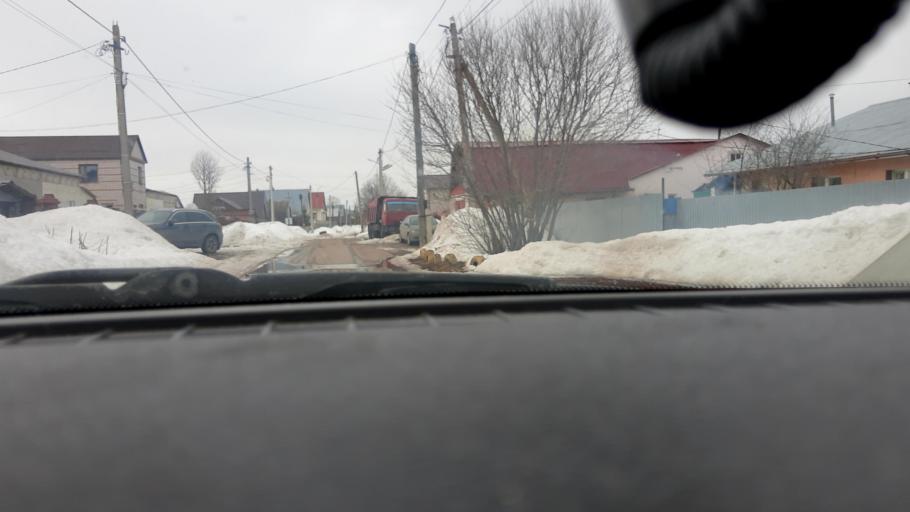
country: RU
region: Bashkortostan
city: Avdon
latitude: 54.6105
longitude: 55.8565
